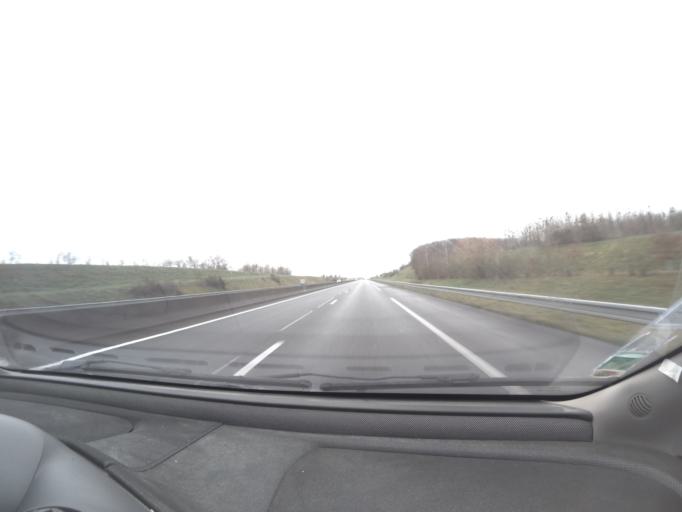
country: FR
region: Pays de la Loire
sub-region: Departement de Maine-et-Loire
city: Saint-Lambert-la-Potherie
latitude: 47.4804
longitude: -0.6676
